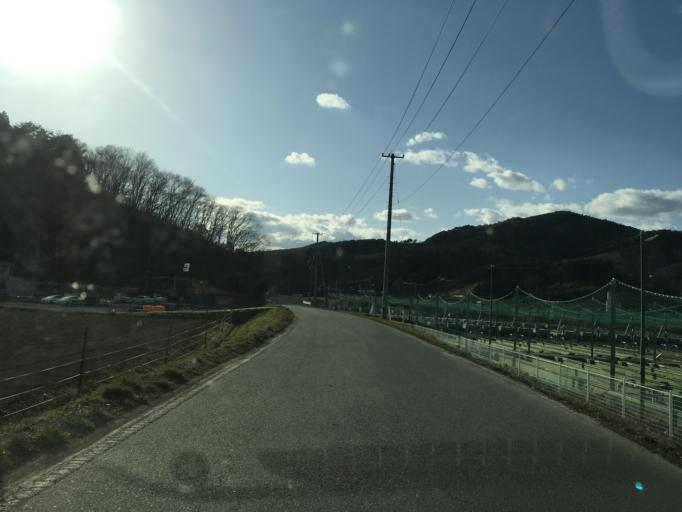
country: JP
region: Iwate
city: Ofunato
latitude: 39.0306
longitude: 141.6056
